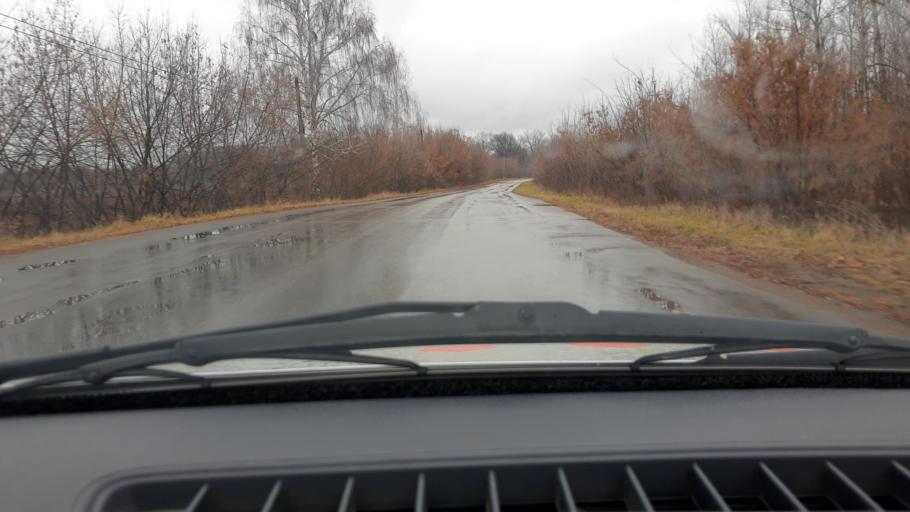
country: RU
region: Bashkortostan
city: Iglino
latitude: 54.8078
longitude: 56.1896
